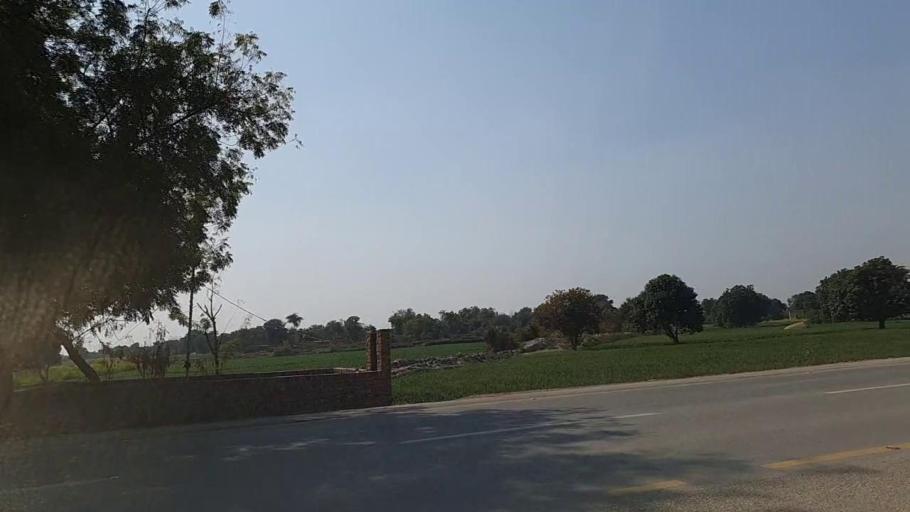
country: PK
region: Sindh
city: Nawabshah
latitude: 26.2443
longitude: 68.4656
